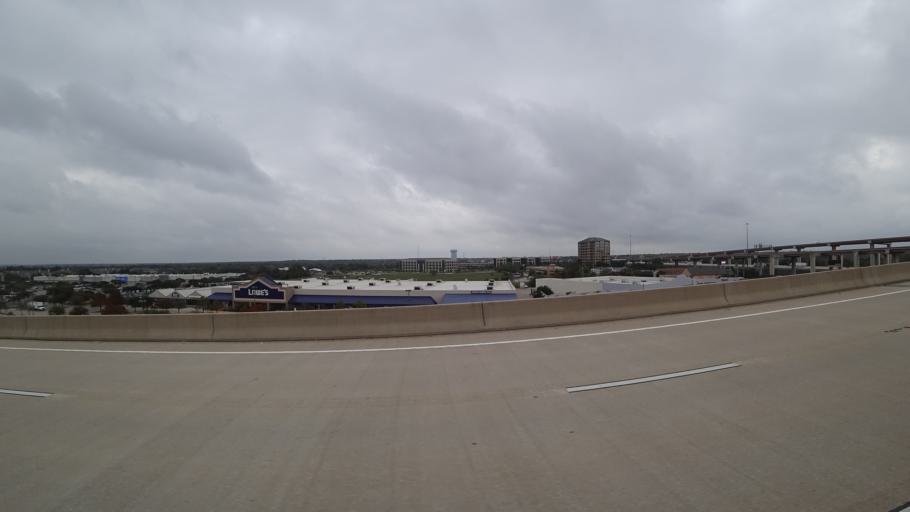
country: US
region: Texas
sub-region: Williamson County
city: Anderson Mill
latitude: 30.4691
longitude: -97.7941
